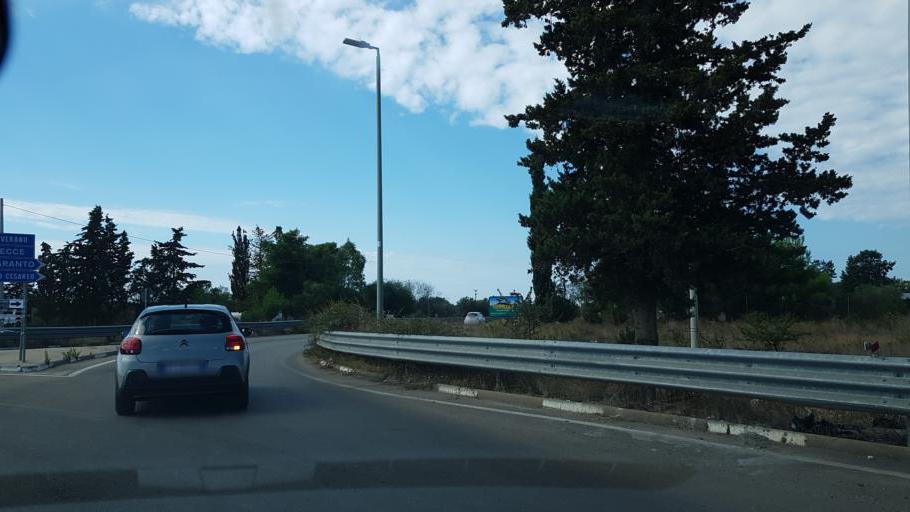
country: IT
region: Apulia
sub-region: Provincia di Lecce
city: Porto Cesareo
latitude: 40.2692
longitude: 17.9179
